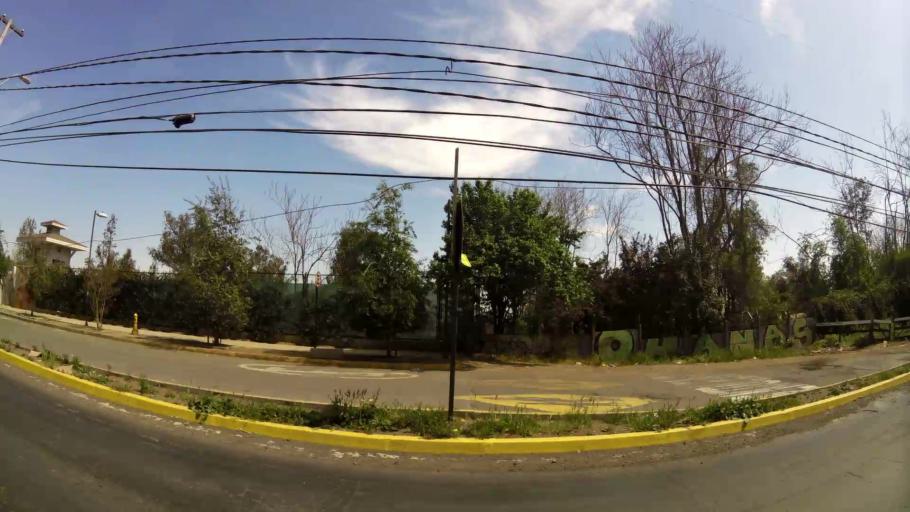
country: CL
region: Santiago Metropolitan
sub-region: Provincia de Santiago
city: Villa Presidente Frei, Nunoa, Santiago, Chile
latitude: -33.4693
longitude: -70.5237
